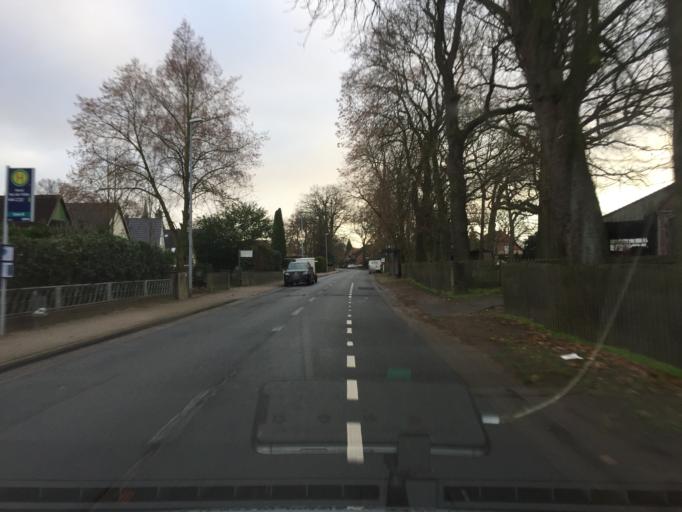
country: DE
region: Lower Saxony
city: Garbsen
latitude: 52.4441
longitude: 9.5316
